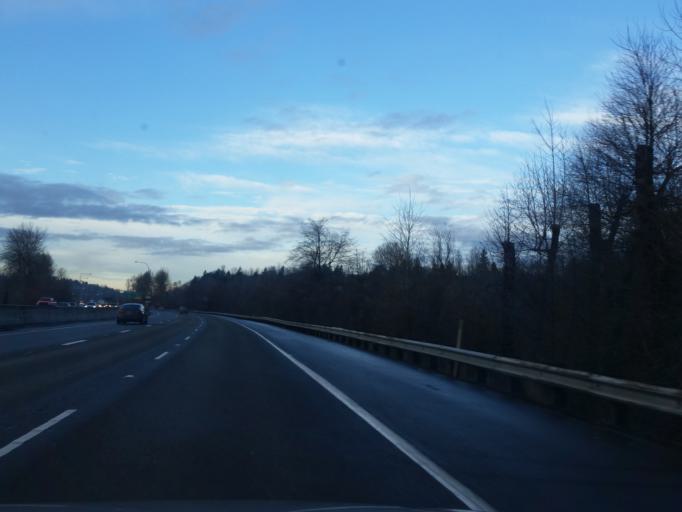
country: US
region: Washington
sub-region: King County
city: Renton
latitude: 47.4507
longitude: -122.2152
